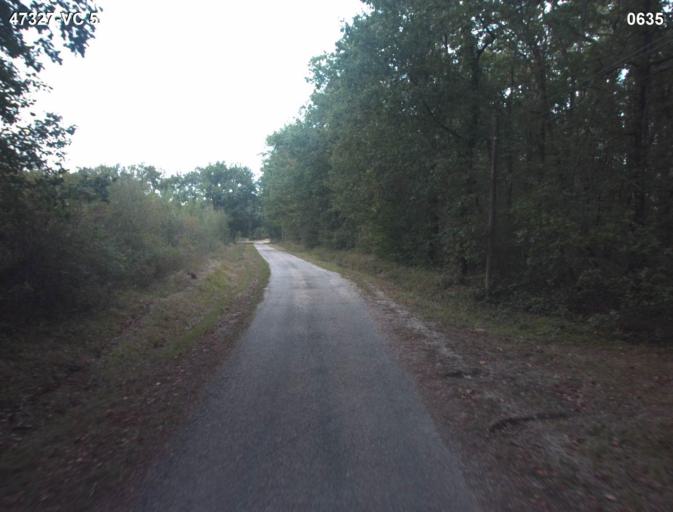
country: FR
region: Aquitaine
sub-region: Departement du Lot-et-Garonne
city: Buzet-sur-Baise
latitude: 44.2220
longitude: 0.2750
